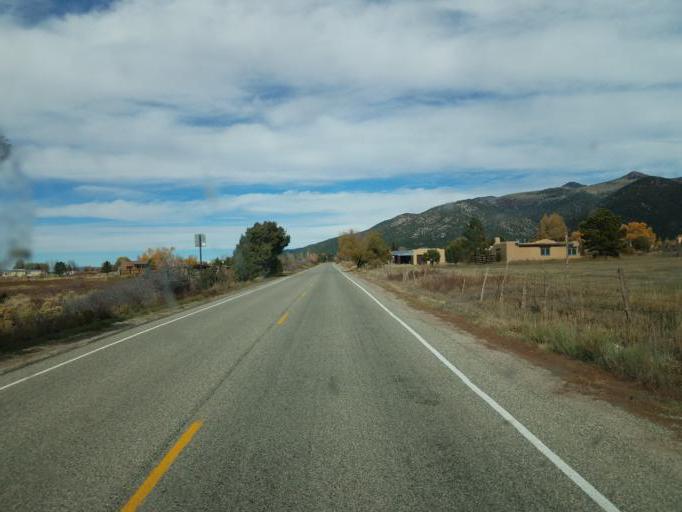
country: US
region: New Mexico
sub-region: Taos County
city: Arroyo Seco
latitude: 36.5216
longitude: -105.5696
